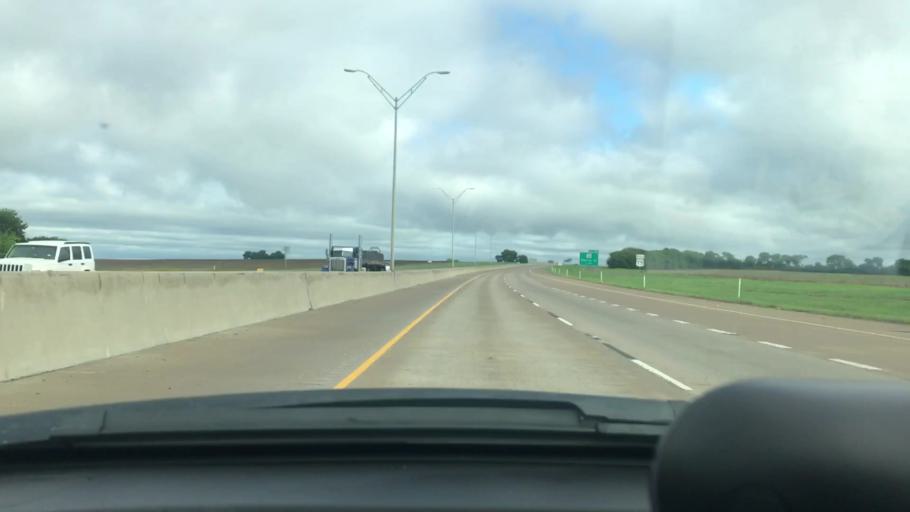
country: US
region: Texas
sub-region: Grayson County
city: Howe
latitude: 33.4733
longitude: -96.6171
